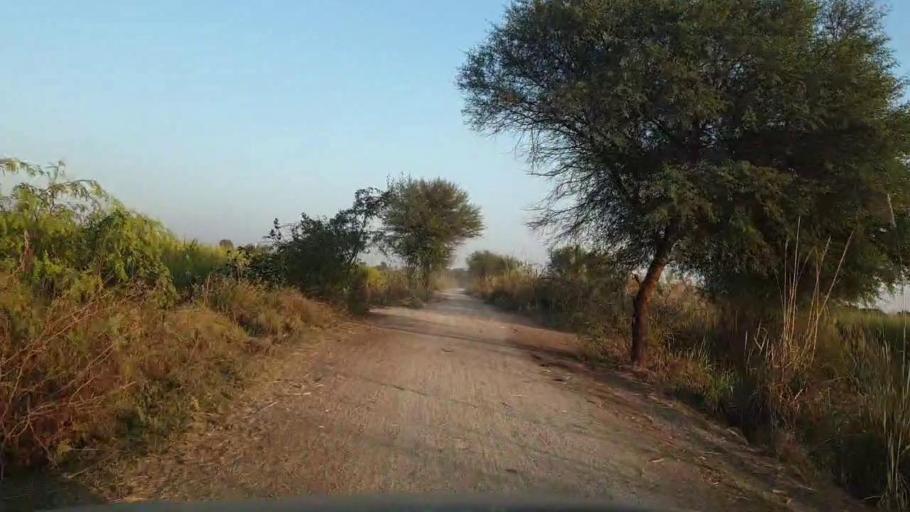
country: PK
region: Sindh
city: Matiari
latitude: 25.6143
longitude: 68.5329
